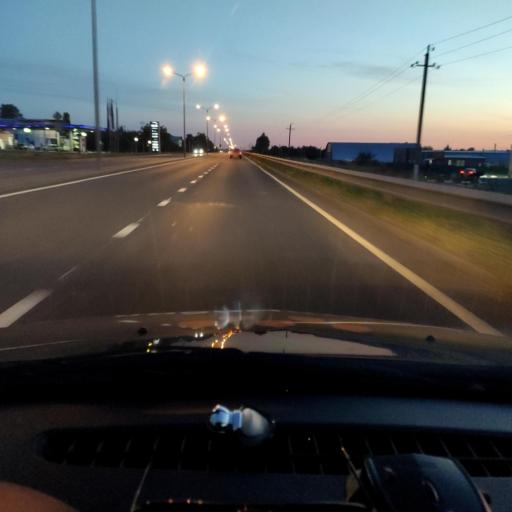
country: RU
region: Belgorod
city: Gubkin
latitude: 51.2643
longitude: 37.5482
